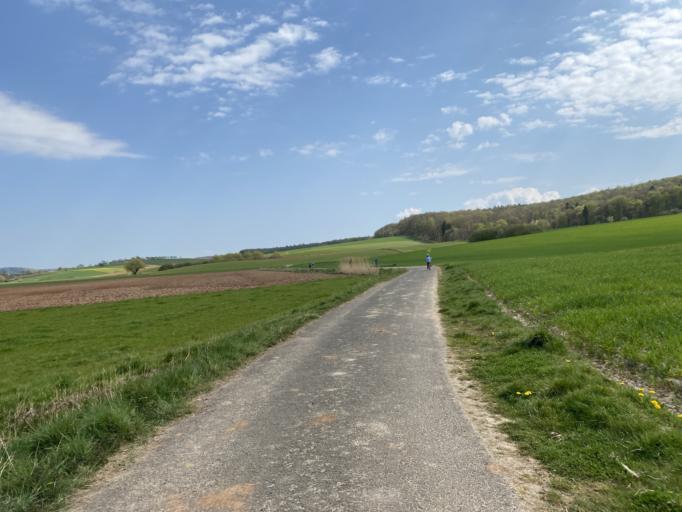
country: DE
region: Hesse
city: Budingen
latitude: 50.2444
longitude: 9.0587
